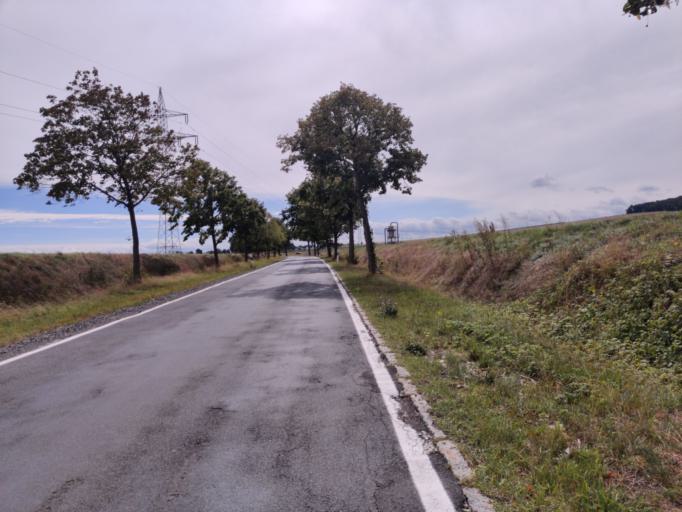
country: DE
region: Lower Saxony
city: Alt Wallmoden
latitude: 52.0176
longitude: 10.3320
